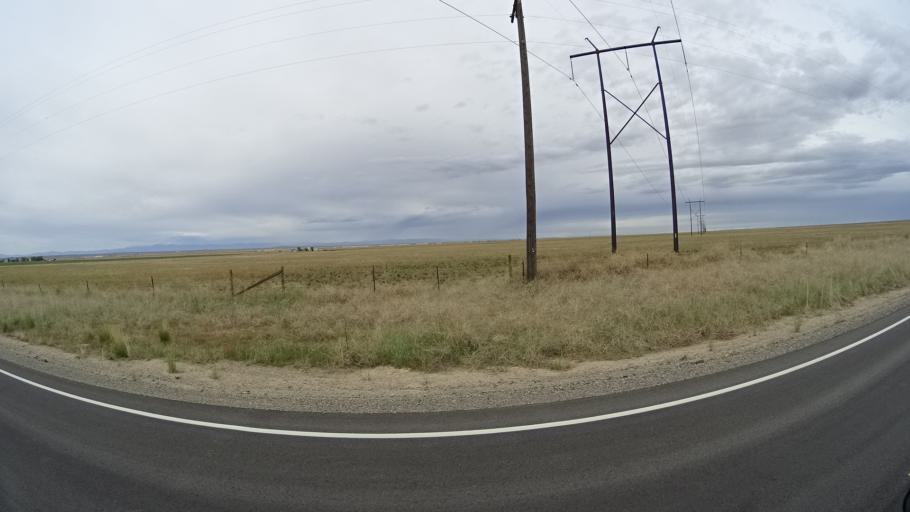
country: US
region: Idaho
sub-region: Elmore County
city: Mountain Home Air Force Base
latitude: 43.3386
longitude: -116.0049
